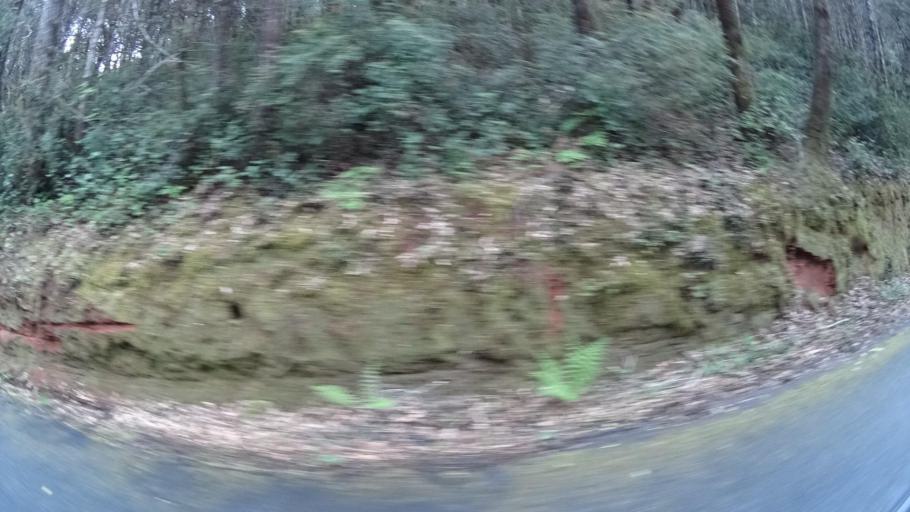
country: US
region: California
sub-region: Humboldt County
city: Willow Creek
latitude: 41.2014
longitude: -123.7655
